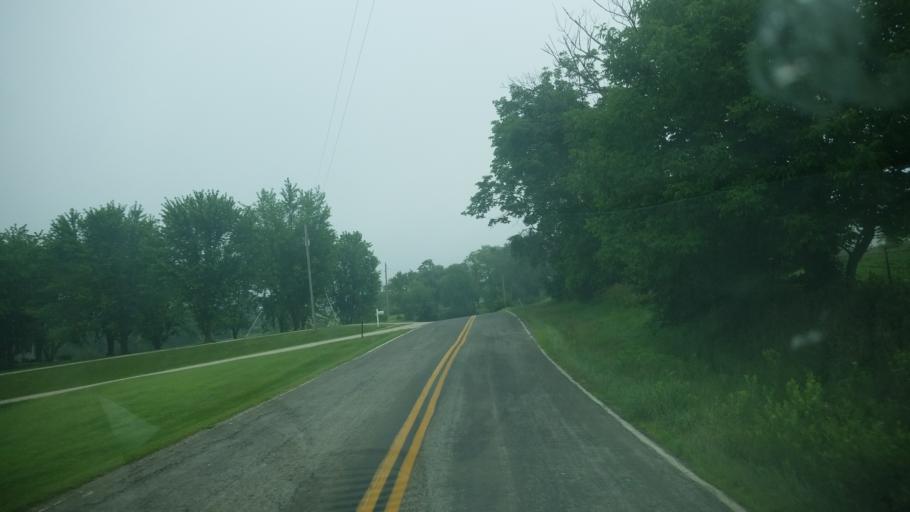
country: US
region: Missouri
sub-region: Audrain County
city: Vandalia
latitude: 39.2796
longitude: -91.3467
